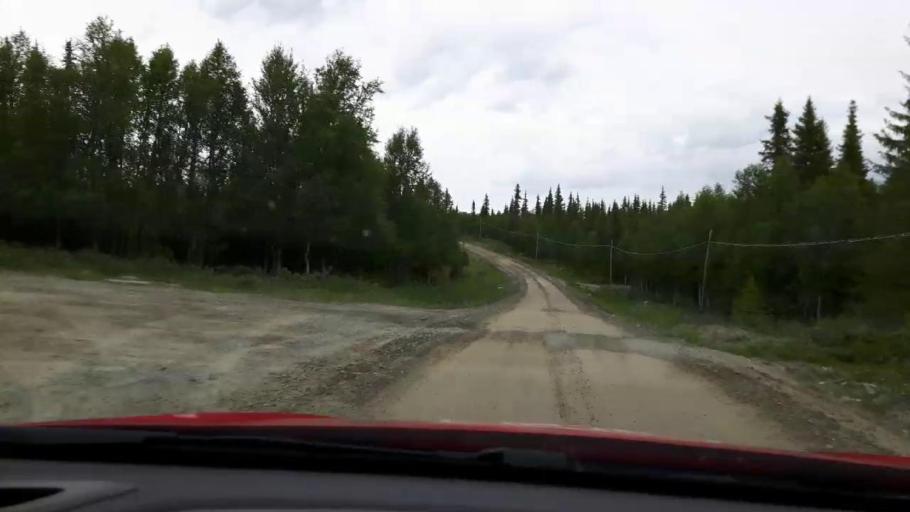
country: SE
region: Jaemtland
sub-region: Are Kommun
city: Are
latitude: 62.8328
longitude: 12.8056
